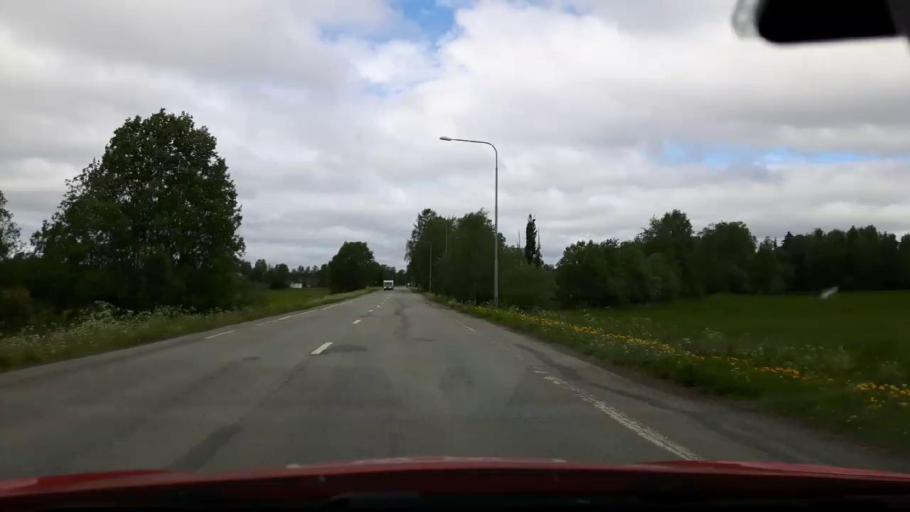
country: SE
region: Jaemtland
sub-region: Krokoms Kommun
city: Krokom
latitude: 63.3067
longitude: 14.4665
